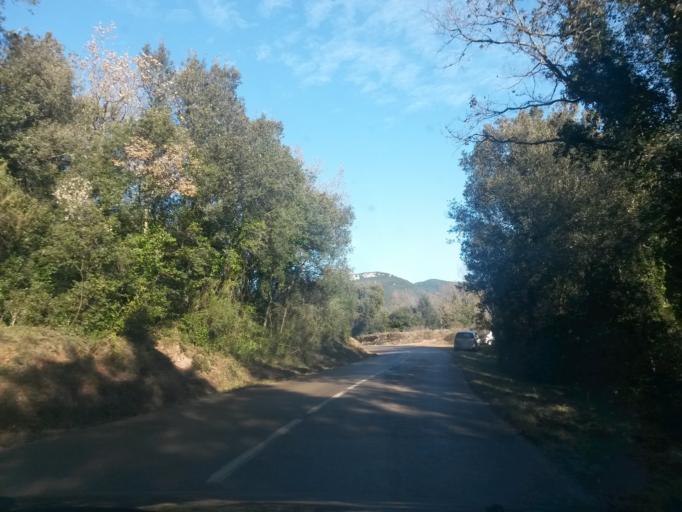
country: ES
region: Catalonia
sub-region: Provincia de Girona
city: la Cellera de Ter
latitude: 42.0182
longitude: 2.6701
